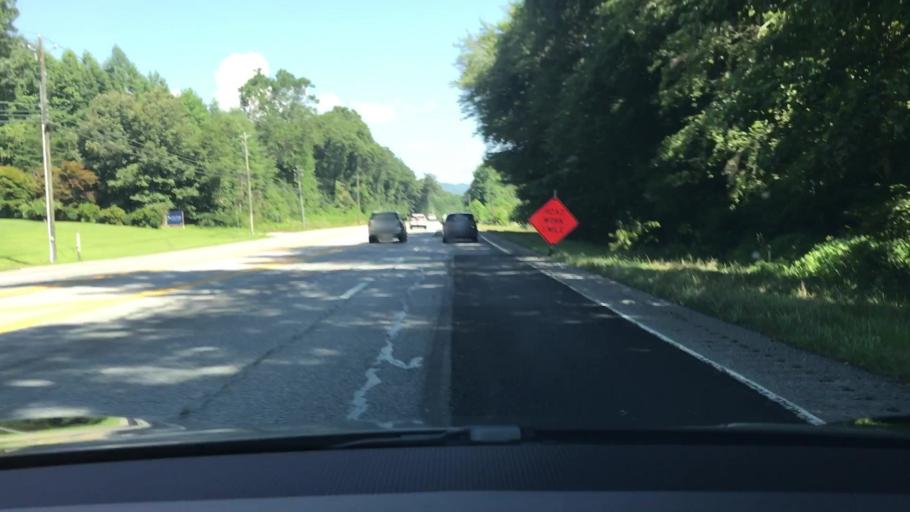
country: US
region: Georgia
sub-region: Rabun County
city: Mountain City
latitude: 34.9272
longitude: -83.3877
